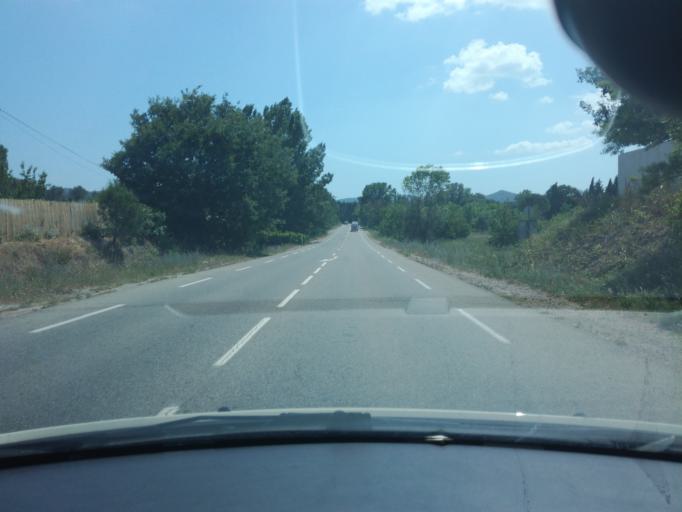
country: FR
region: Provence-Alpes-Cote d'Azur
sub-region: Departement du Var
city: Le Muy
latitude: 43.4840
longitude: 6.5666
